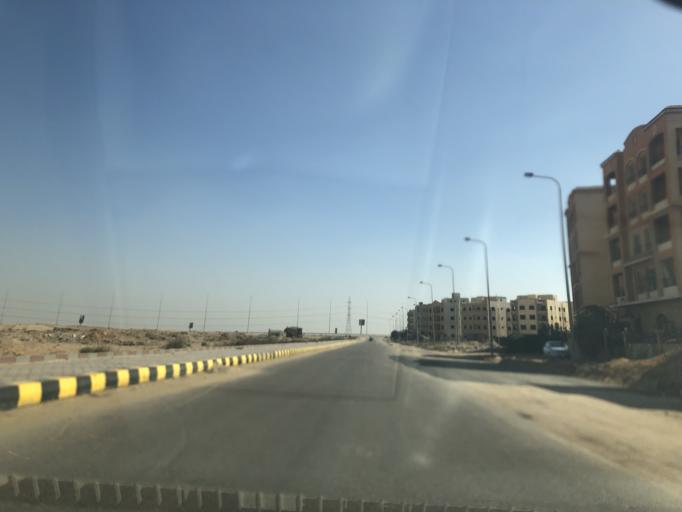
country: EG
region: Al Jizah
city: Madinat Sittah Uktubar
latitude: 29.9011
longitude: 31.0803
